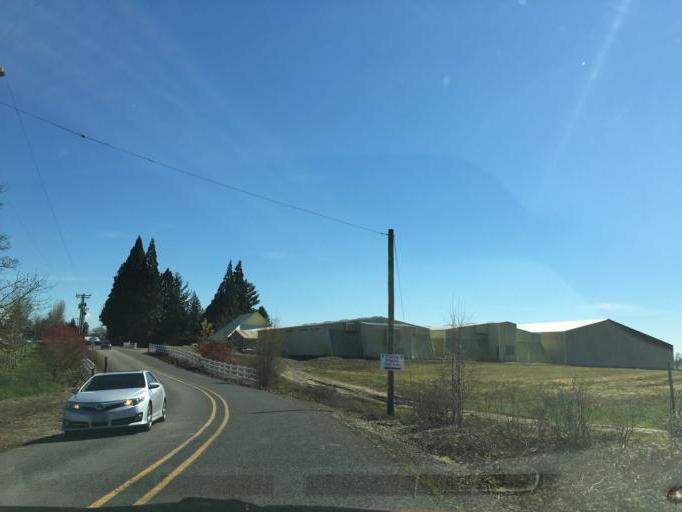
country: US
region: Oregon
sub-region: Marion County
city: Mount Angel
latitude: 45.1197
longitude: -122.7526
